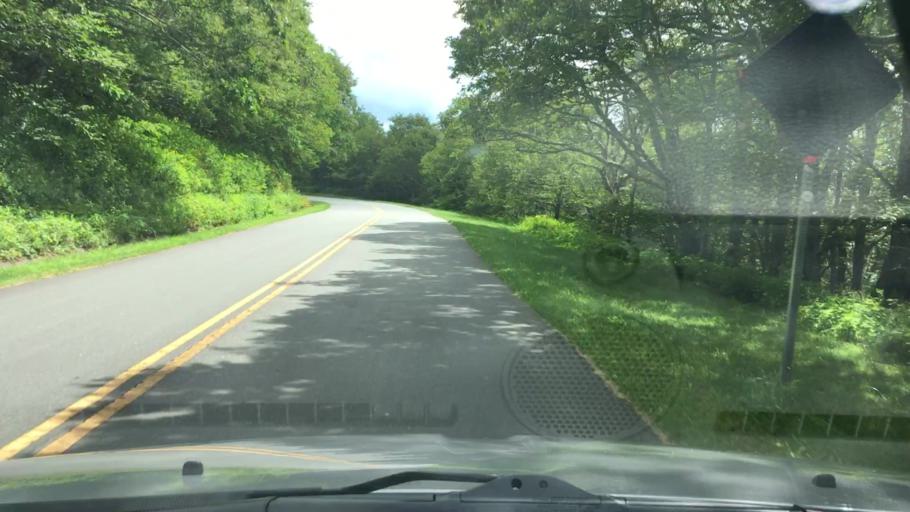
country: US
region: North Carolina
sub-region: Buncombe County
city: Swannanoa
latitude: 35.6830
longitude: -82.3878
